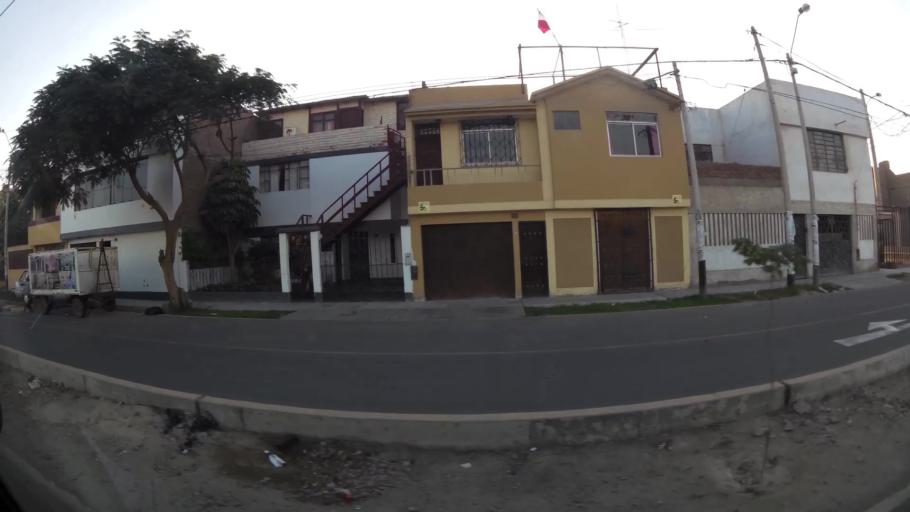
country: PE
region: Ica
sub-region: Provincia de Ica
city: Ica
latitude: -14.0851
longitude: -75.7229
